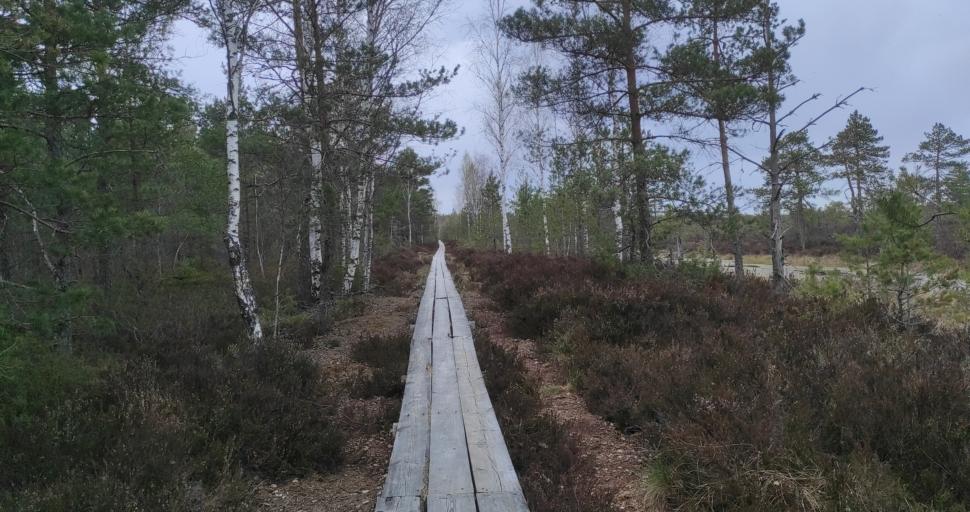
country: LV
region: Dundaga
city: Dundaga
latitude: 57.3496
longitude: 22.1500
